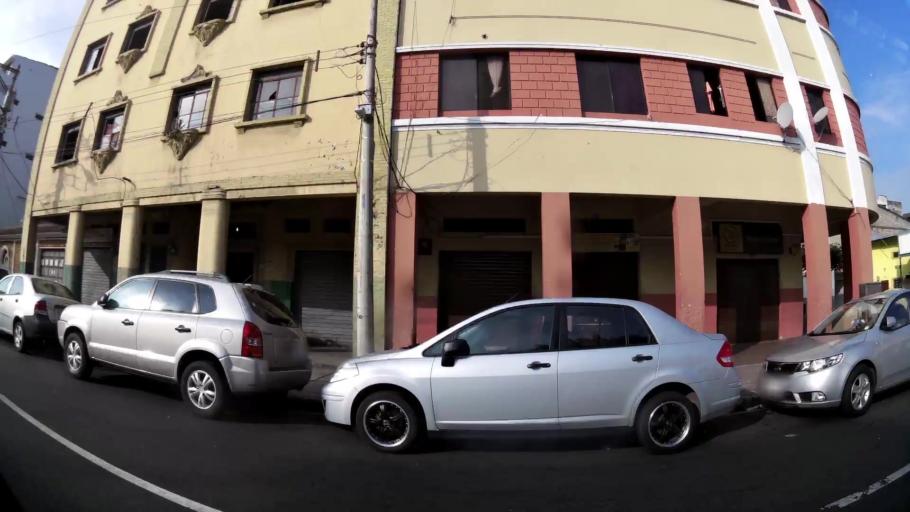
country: EC
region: Guayas
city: Guayaquil
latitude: -2.2012
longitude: -79.8881
